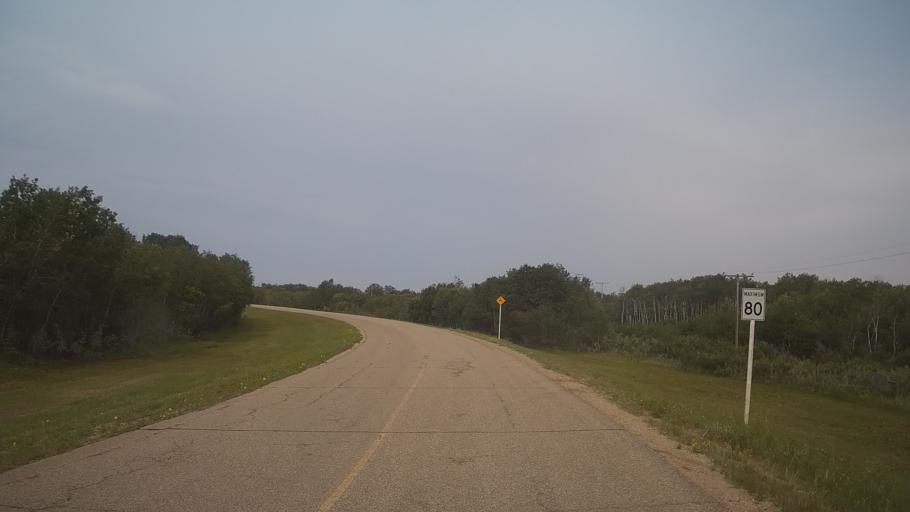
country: CA
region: Saskatchewan
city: Saskatoon
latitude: 51.8529
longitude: -106.5245
